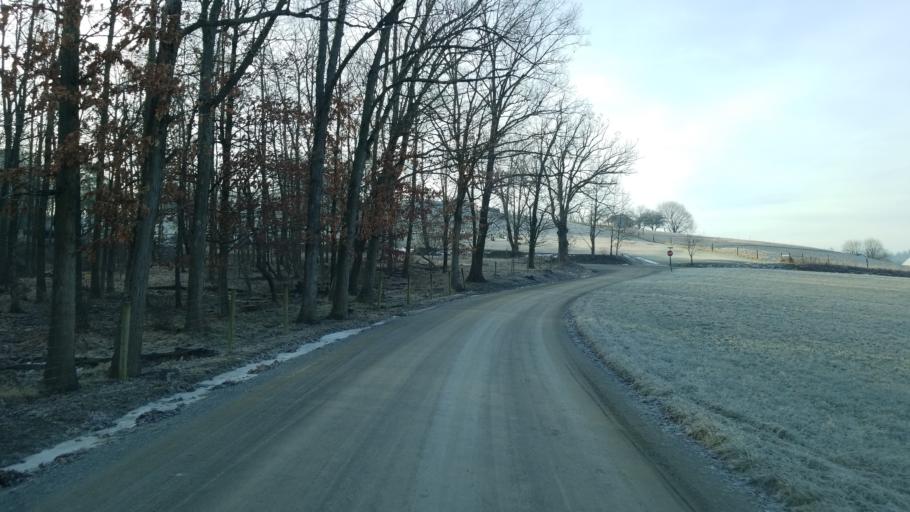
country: US
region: Pennsylvania
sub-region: Indiana County
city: Chevy Chase Heights
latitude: 40.8733
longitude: -79.2344
